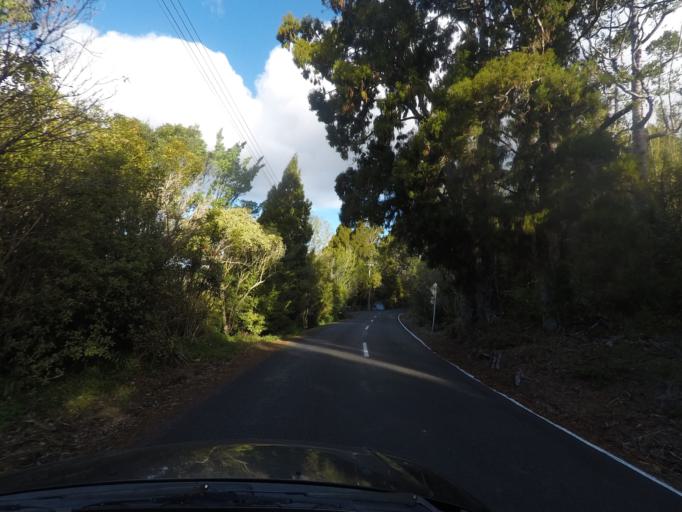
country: NZ
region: Auckland
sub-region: Auckland
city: Titirangi
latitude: -36.9316
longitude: 174.6190
